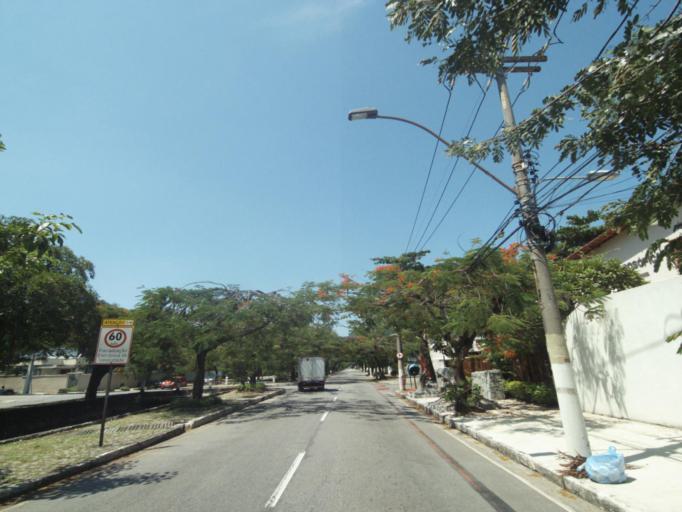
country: BR
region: Rio de Janeiro
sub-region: Niteroi
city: Niteroi
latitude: -22.9145
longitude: -43.0913
